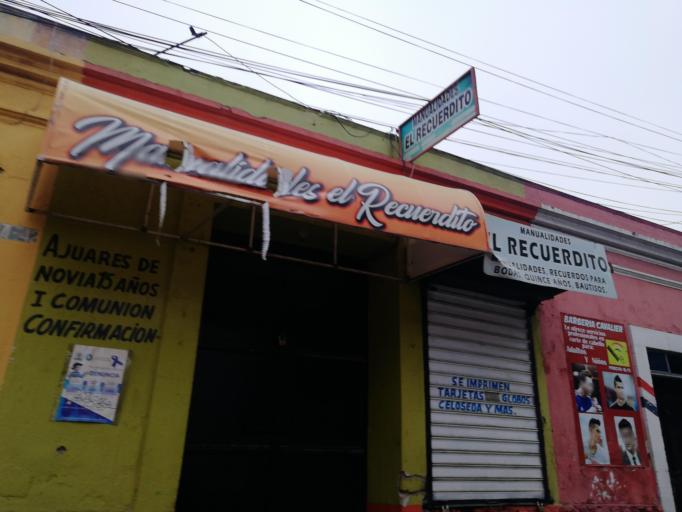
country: GT
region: Quetzaltenango
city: Quetzaltenango
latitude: 14.8401
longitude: -91.5193
